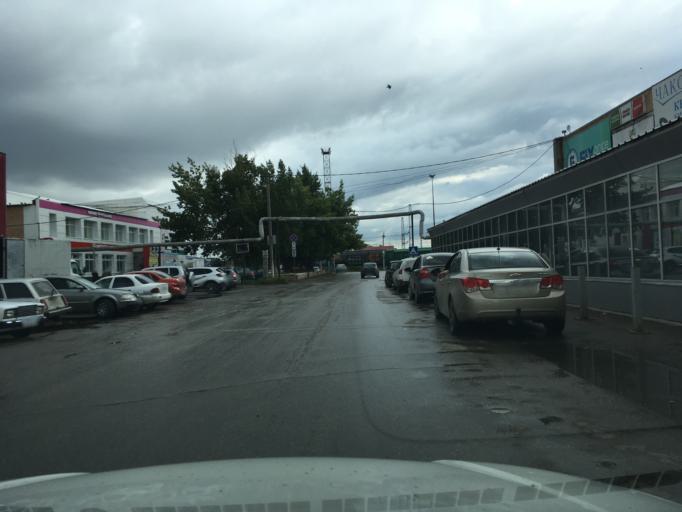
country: RU
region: Samara
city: Bezenchuk
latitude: 52.9802
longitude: 49.4318
